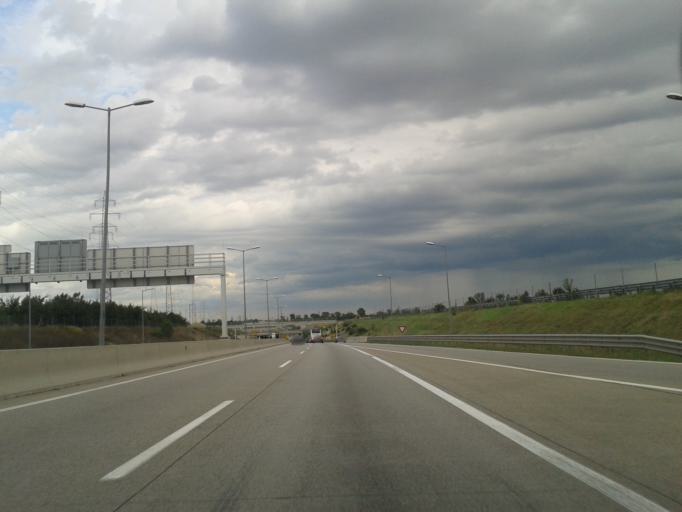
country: AT
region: Lower Austria
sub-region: Politischer Bezirk Modling
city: Hennersdorf
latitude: 48.1290
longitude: 16.3581
